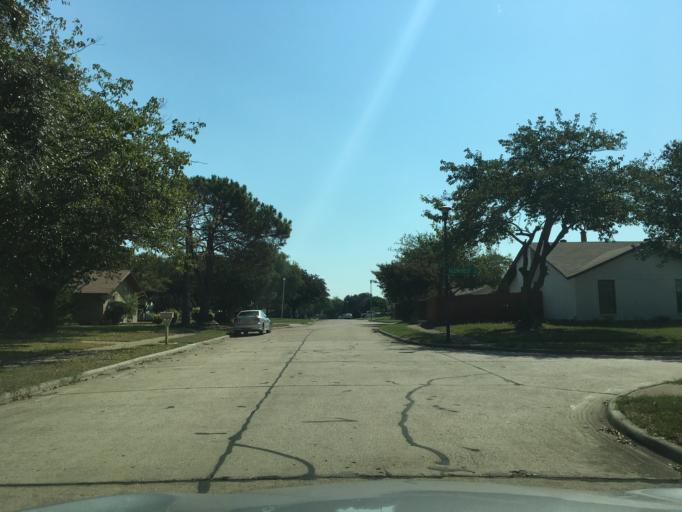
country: US
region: Texas
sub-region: Dallas County
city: Garland
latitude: 32.9335
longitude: -96.6358
